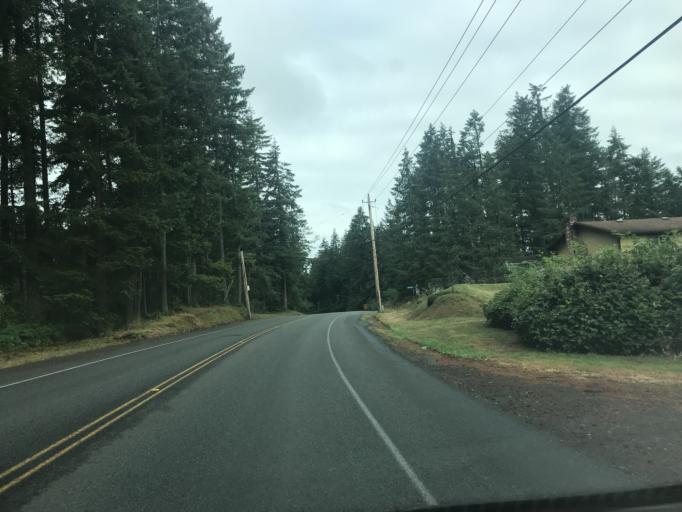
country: US
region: Washington
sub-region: King County
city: Lake Morton-Berrydale
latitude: 47.3419
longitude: -122.0616
